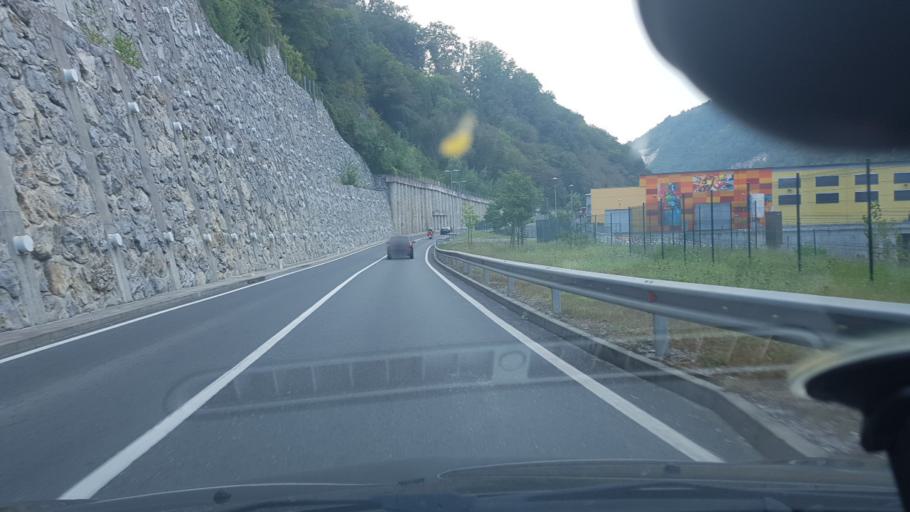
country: SI
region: Krsko
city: Krsko
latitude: 45.9734
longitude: 15.4818
